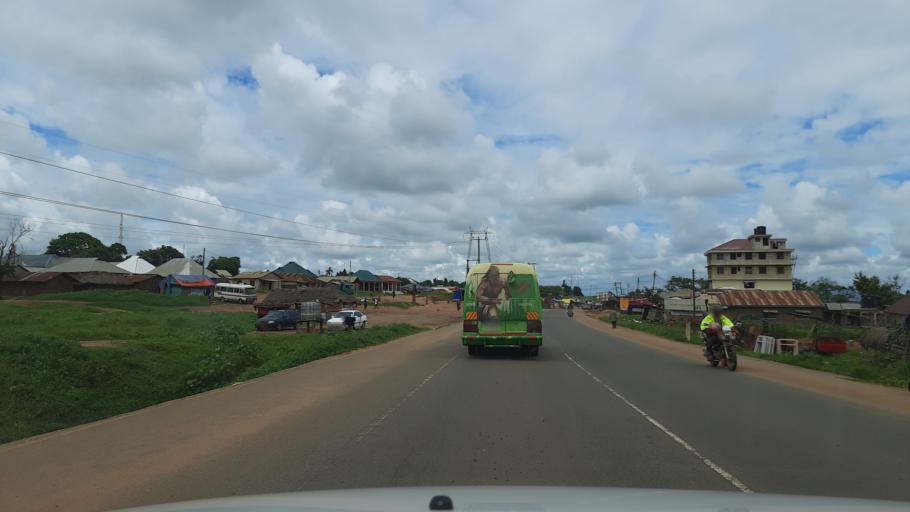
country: TZ
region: Tanga
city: Chanika
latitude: -5.7884
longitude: 38.2903
